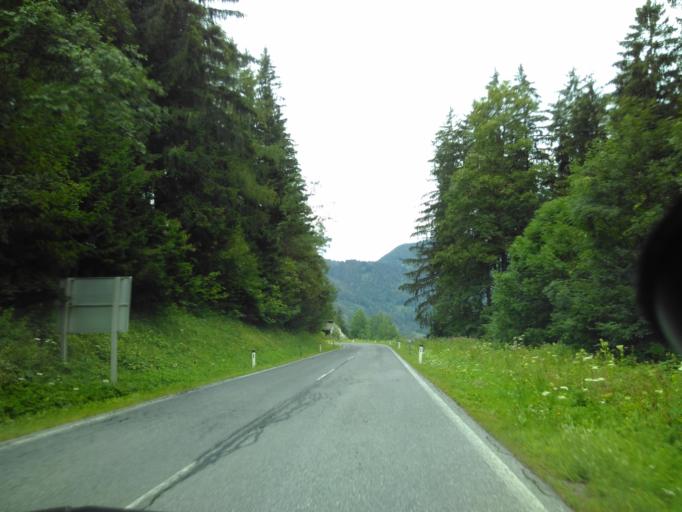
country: AT
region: Styria
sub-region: Politischer Bezirk Graz-Umgebung
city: Semriach
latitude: 47.2691
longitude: 15.4123
